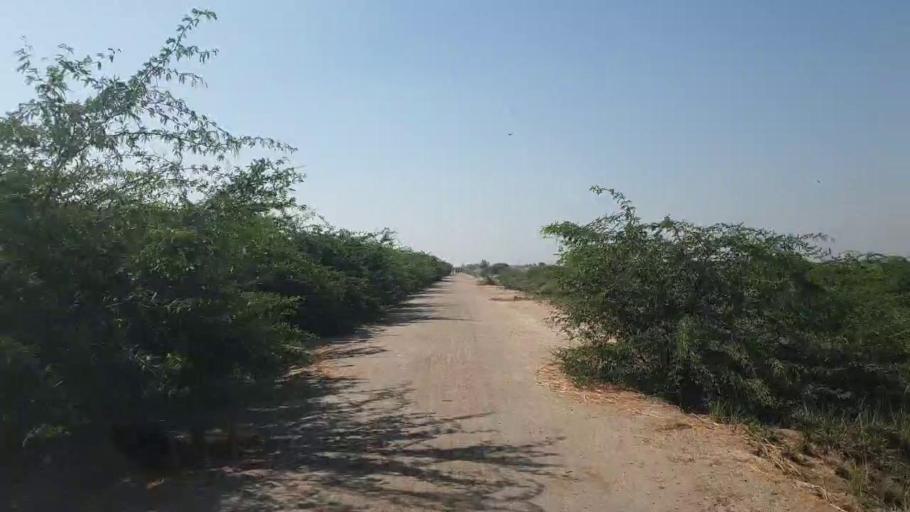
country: PK
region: Sindh
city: Talhar
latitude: 24.8264
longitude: 68.7696
